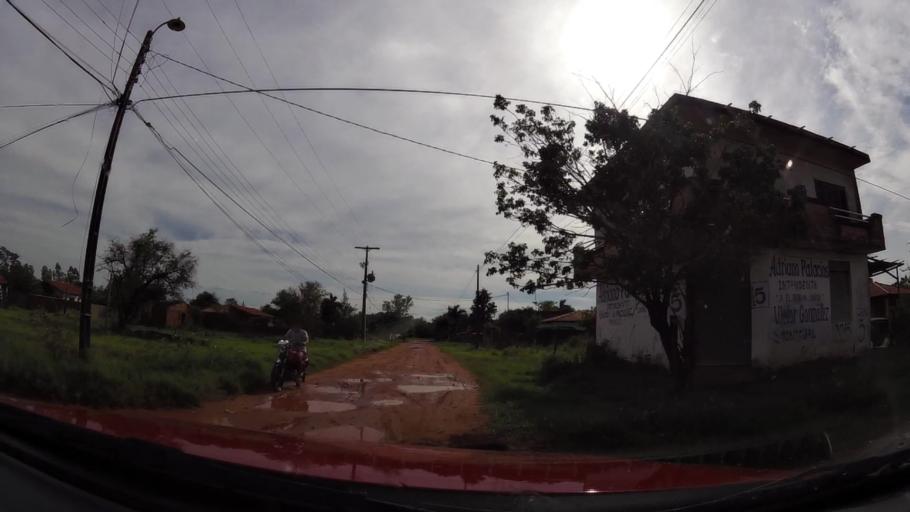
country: PY
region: Central
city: Limpio
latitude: -25.1789
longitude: -57.4938
